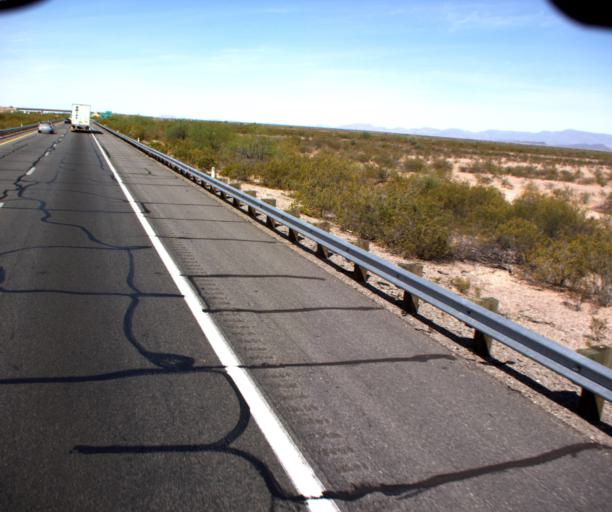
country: US
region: Arizona
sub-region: La Paz County
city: Salome
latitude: 33.5359
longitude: -113.1463
